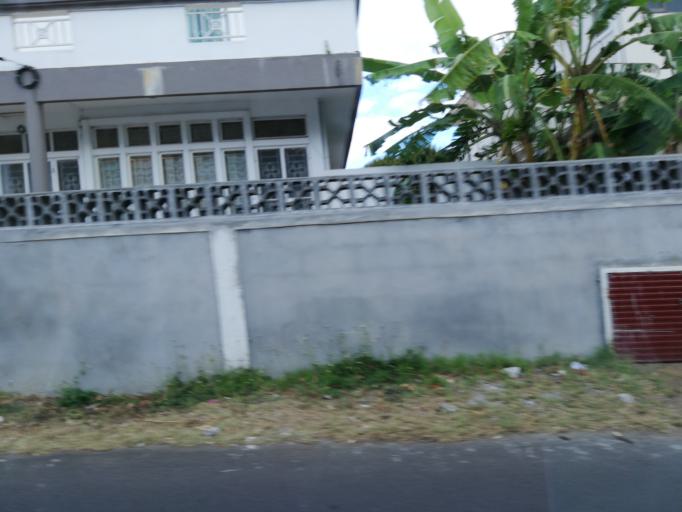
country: MU
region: Plaines Wilhems
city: Quatre Bornes
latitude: -20.2361
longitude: 57.4565
